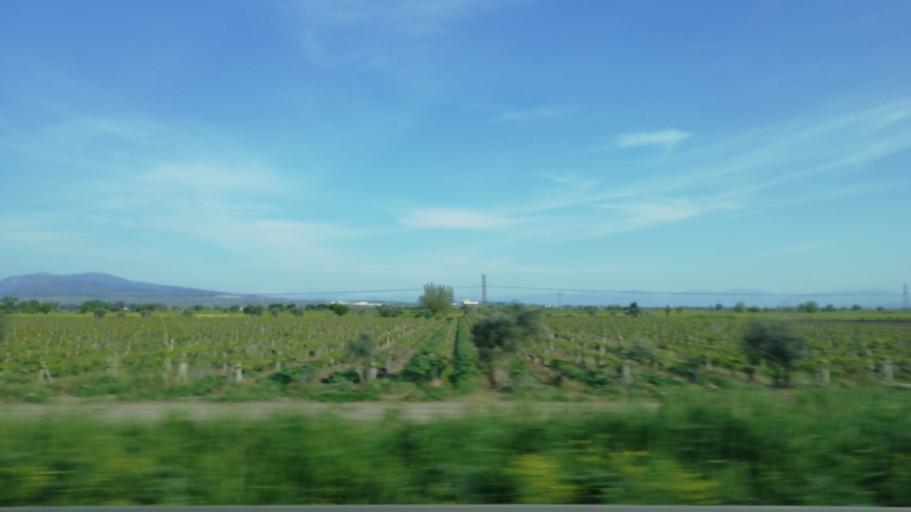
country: TR
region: Manisa
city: Saruhanli
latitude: 38.7224
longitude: 27.5653
